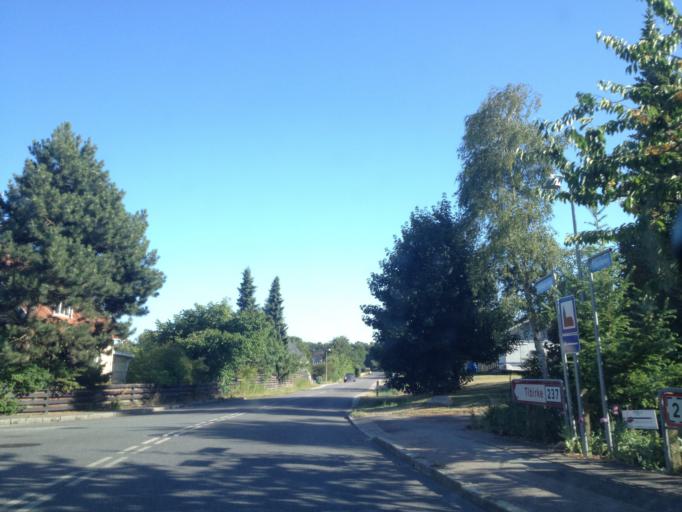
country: DK
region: Capital Region
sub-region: Gribskov Kommune
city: Helsinge
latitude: 56.0512
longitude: 12.1093
